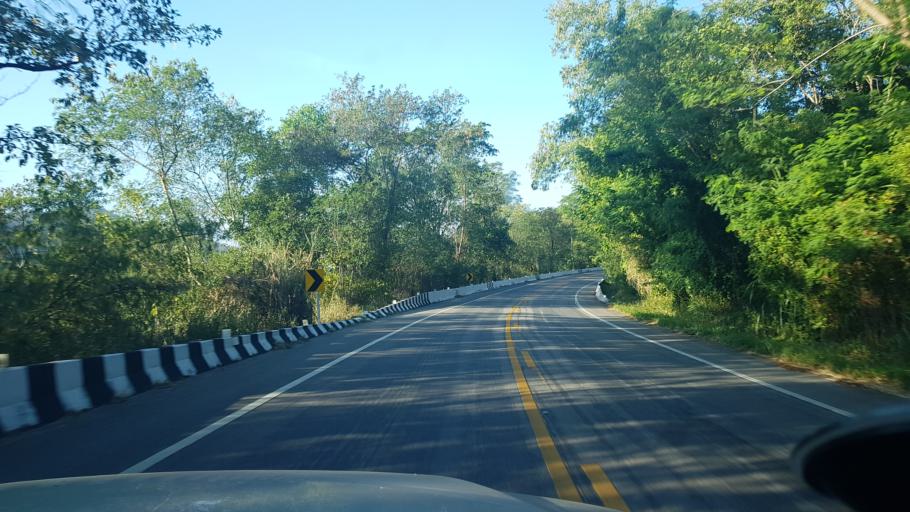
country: TH
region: Khon Kaen
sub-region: Amphoe Phu Pha Man
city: Phu Pha Man
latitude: 16.6466
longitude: 101.7932
